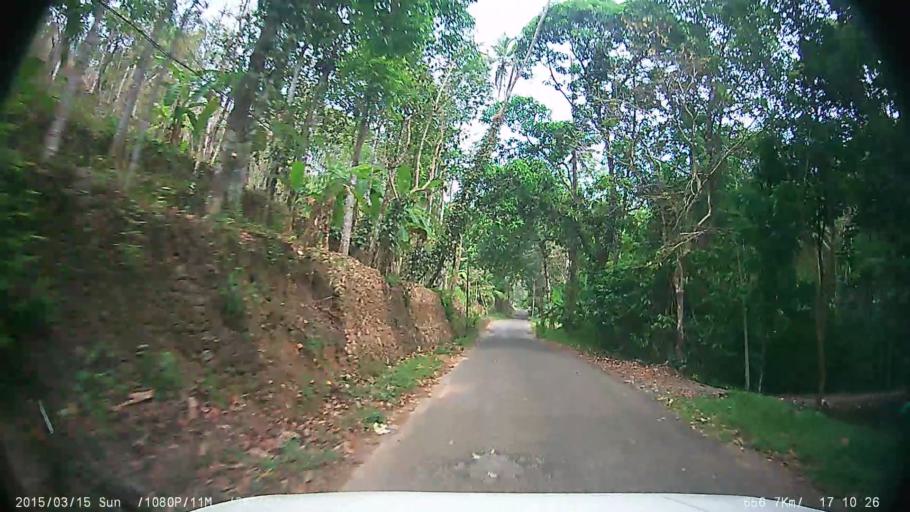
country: IN
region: Kerala
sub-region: Kottayam
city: Palackattumala
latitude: 9.8606
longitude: 76.6745
